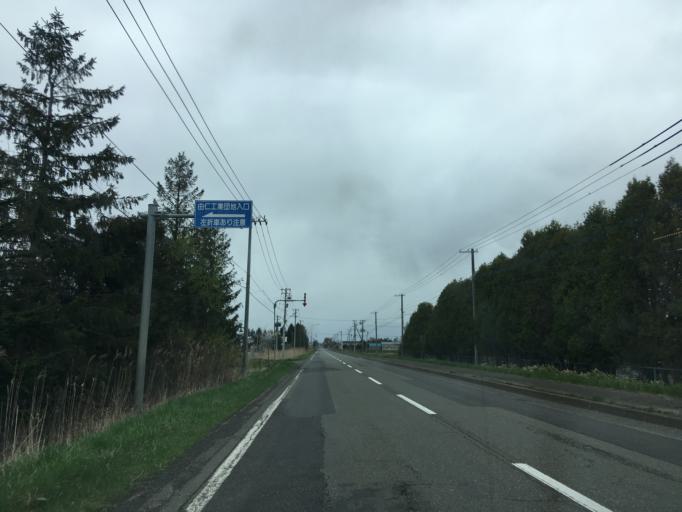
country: JP
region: Hokkaido
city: Chitose
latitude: 42.9316
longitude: 141.8067
